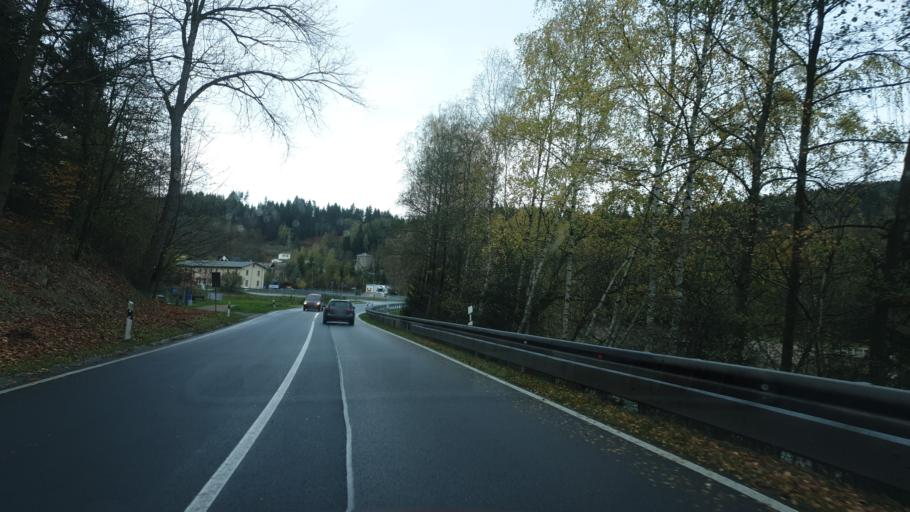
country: DE
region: Saxony
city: Schoenheide
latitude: 50.5041
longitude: 12.5590
